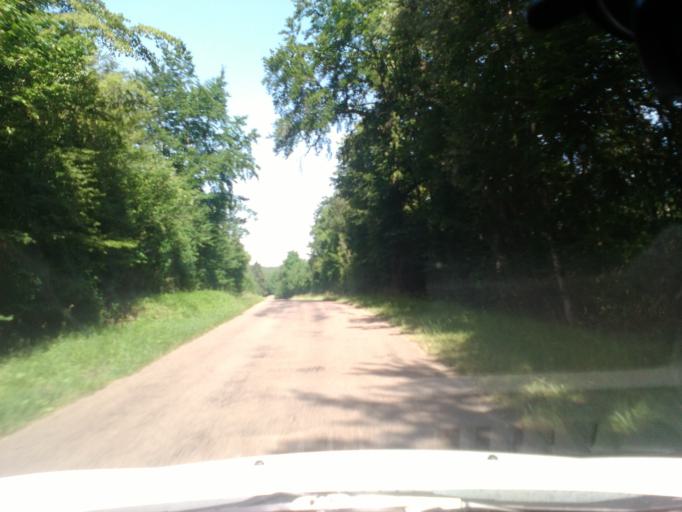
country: FR
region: Lorraine
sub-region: Departement des Vosges
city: Liffol-le-Grand
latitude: 48.2989
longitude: 5.4645
